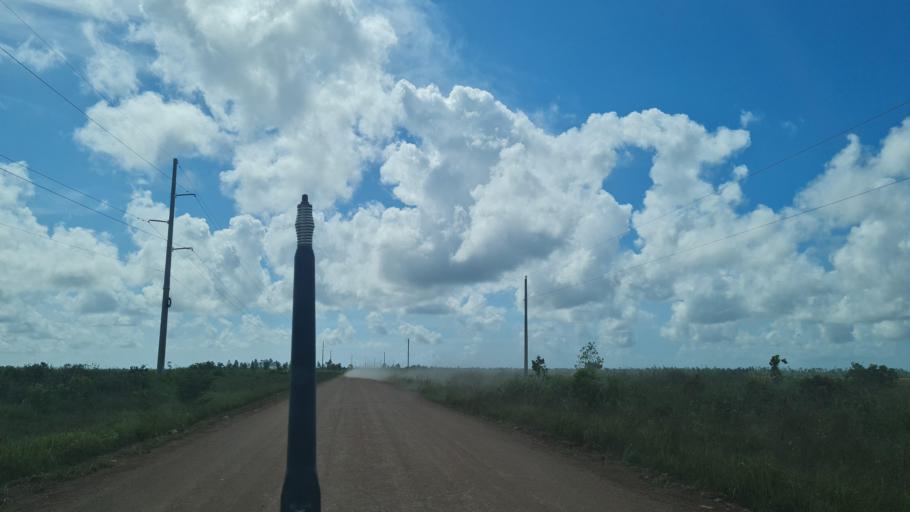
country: NI
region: Atlantico Norte (RAAN)
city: Puerto Cabezas
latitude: 14.1087
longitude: -83.5736
